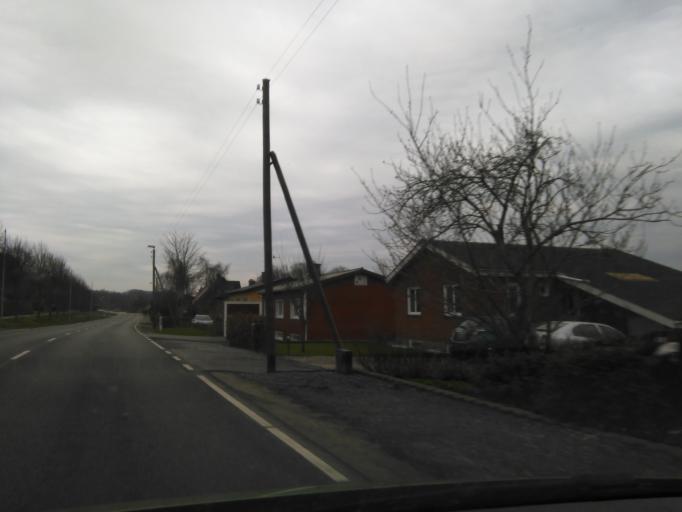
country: DK
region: North Denmark
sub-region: Mariagerfjord Kommune
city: Hadsund
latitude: 56.7031
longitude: 10.1152
